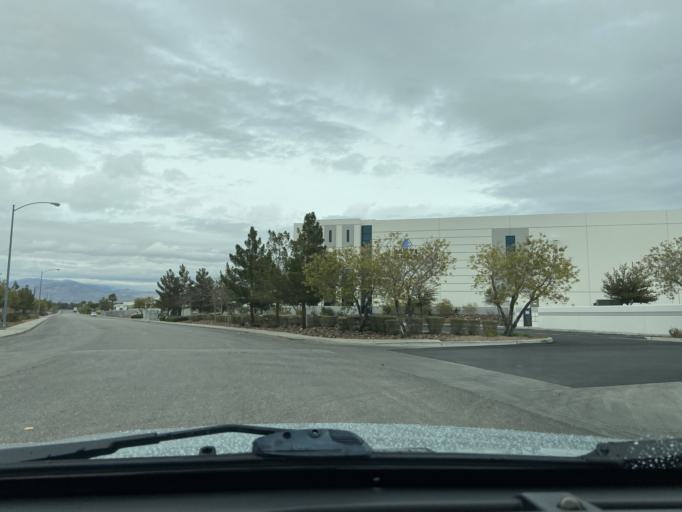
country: US
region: Nevada
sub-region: Clark County
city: Sunrise Manor
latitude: 36.2443
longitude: -115.1045
